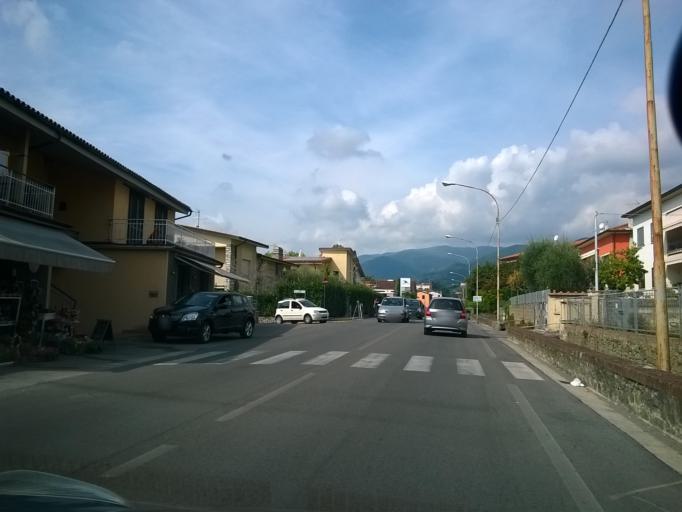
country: IT
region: Tuscany
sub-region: Provincia di Pistoia
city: Santa Lucia
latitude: 43.8852
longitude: 10.6999
